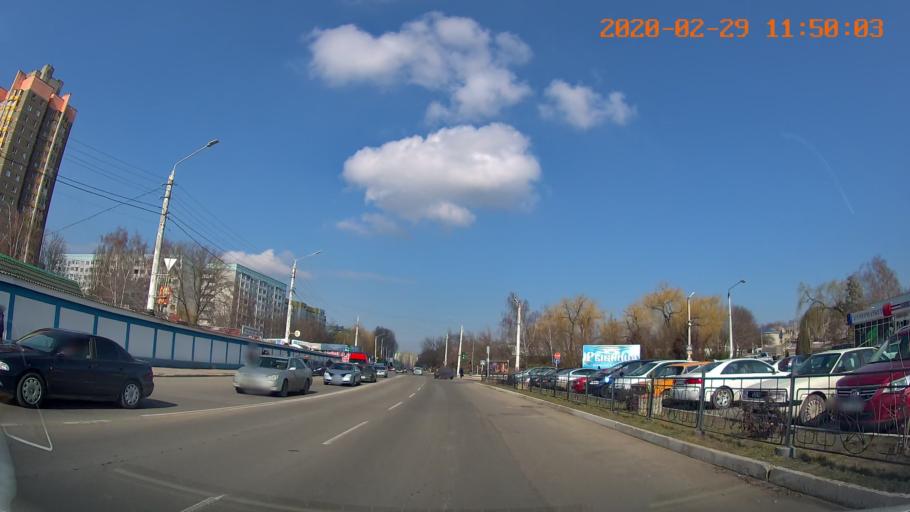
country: MD
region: Telenesti
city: Ribnita
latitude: 47.7554
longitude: 28.9916
